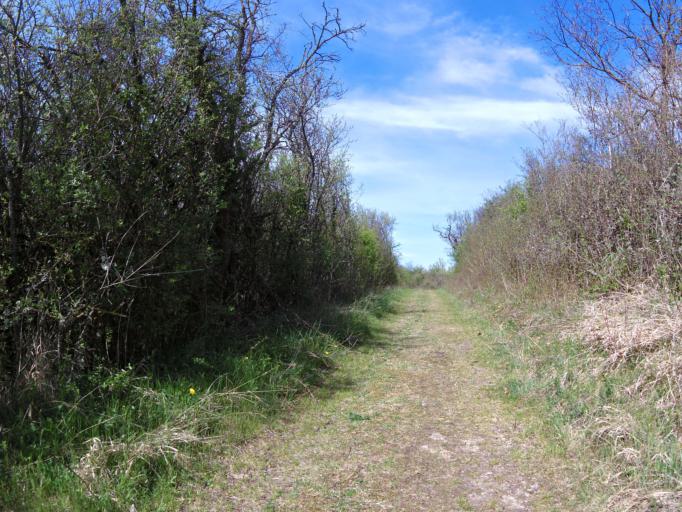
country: DE
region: Bavaria
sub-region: Regierungsbezirk Unterfranken
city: Rimpar
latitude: 49.8576
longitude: 9.9699
